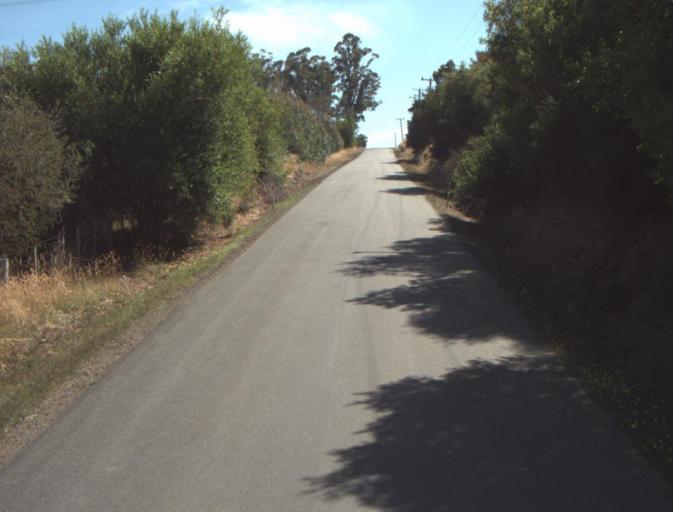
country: AU
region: Tasmania
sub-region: Launceston
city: Mayfield
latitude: -41.2362
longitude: 147.2342
